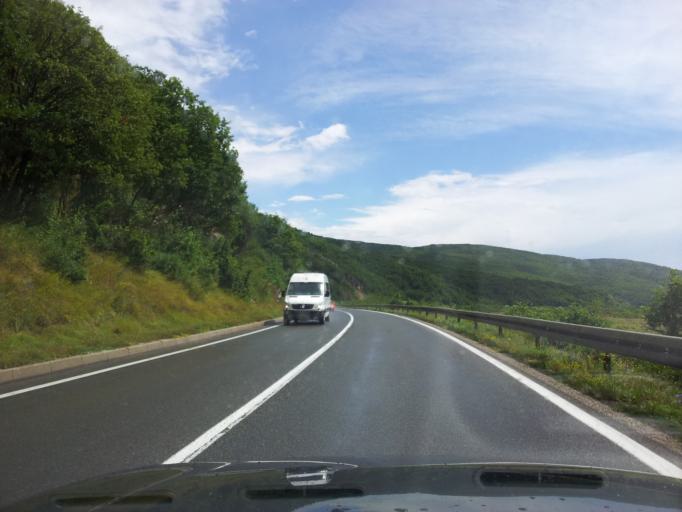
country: BA
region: Federation of Bosnia and Herzegovina
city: Bihac
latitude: 44.6283
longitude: 15.7321
